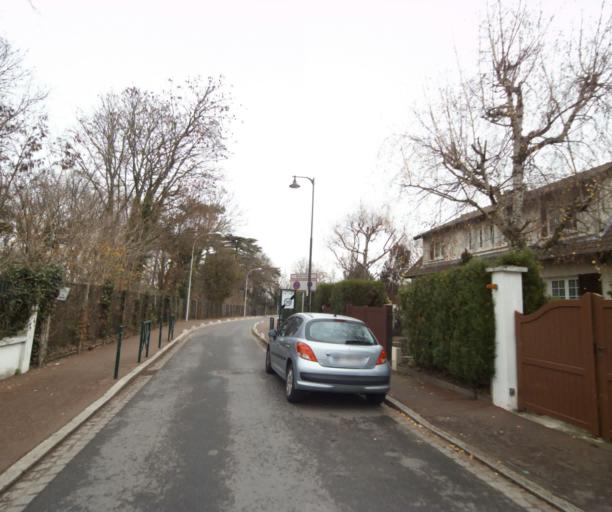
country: FR
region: Ile-de-France
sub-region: Departement des Hauts-de-Seine
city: Rueil-Malmaison
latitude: 48.8798
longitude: 2.1991
